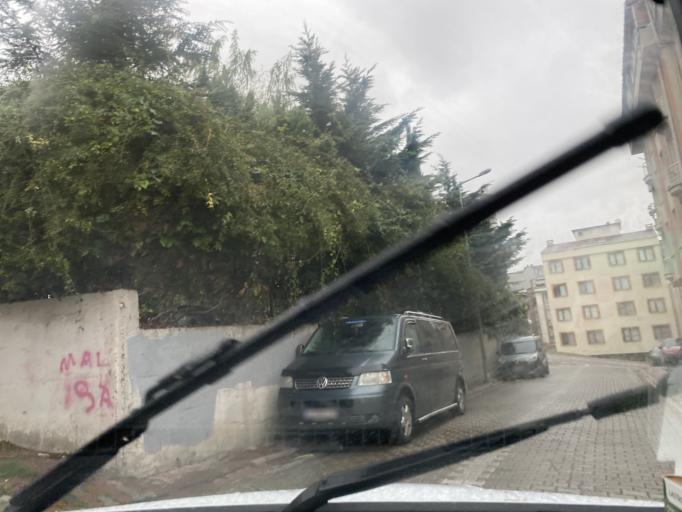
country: TR
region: Istanbul
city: Esenyurt
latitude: 41.0212
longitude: 28.6621
